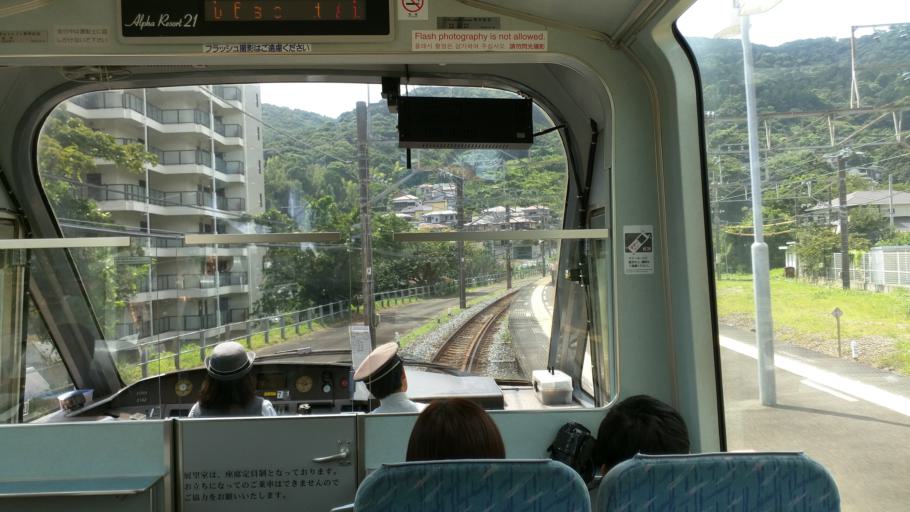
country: JP
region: Shizuoka
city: Atami
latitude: 35.0447
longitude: 139.0801
